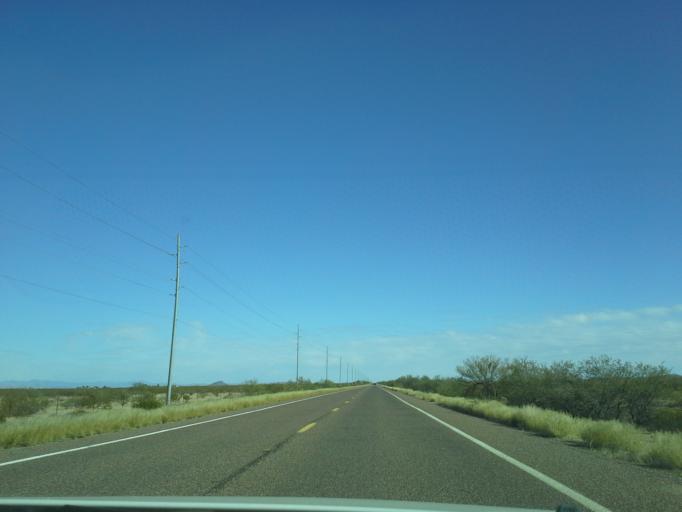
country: US
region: Arizona
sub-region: Yavapai County
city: Congress
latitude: 33.9429
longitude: -113.0686
